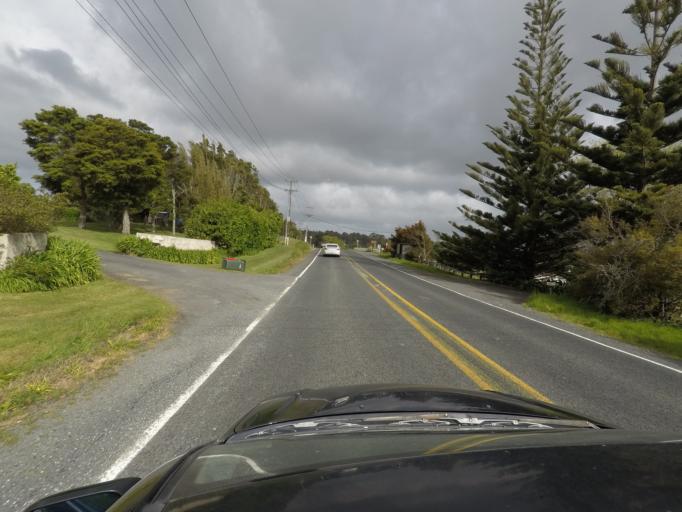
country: NZ
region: Auckland
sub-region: Auckland
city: Pakuranga
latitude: -36.9345
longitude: 174.9390
